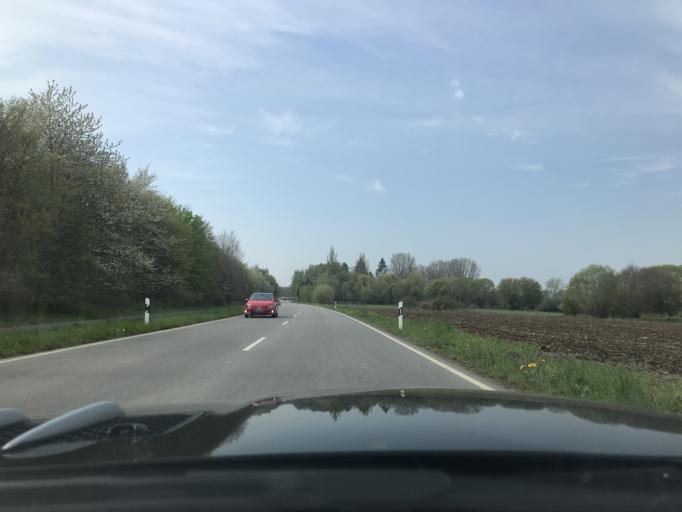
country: DE
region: Schleswig-Holstein
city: Grube
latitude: 54.2022
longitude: 11.0307
